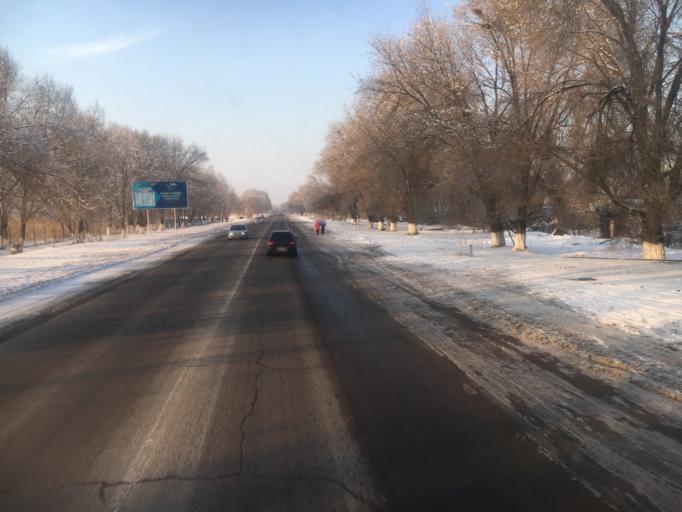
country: KZ
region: Almaty Oblysy
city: Burunday
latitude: 43.3354
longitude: 76.6603
